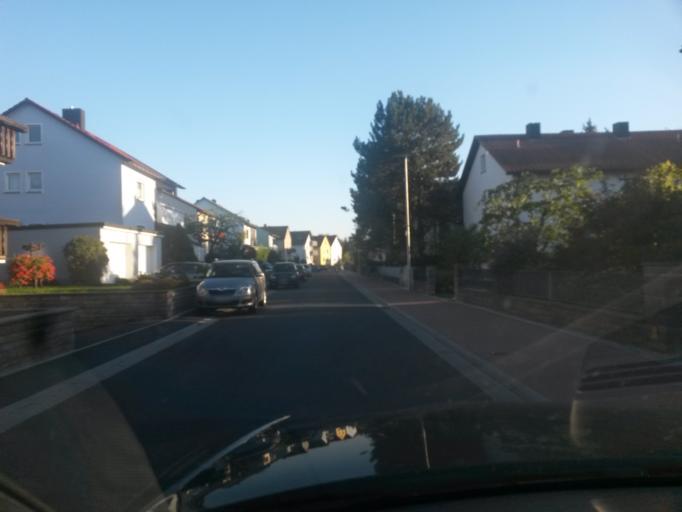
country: DE
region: Bavaria
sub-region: Regierungsbezirk Unterfranken
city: Rimpar
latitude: 49.8536
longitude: 9.9648
